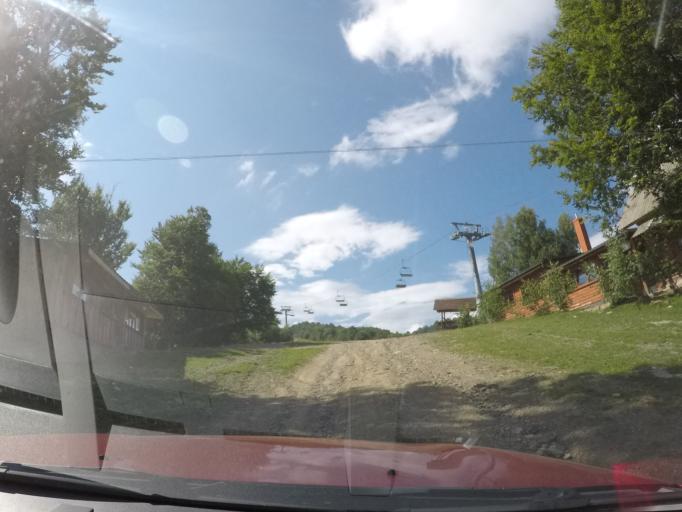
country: UA
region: Zakarpattia
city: Velykyi Bereznyi
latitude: 48.9354
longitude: 22.6675
